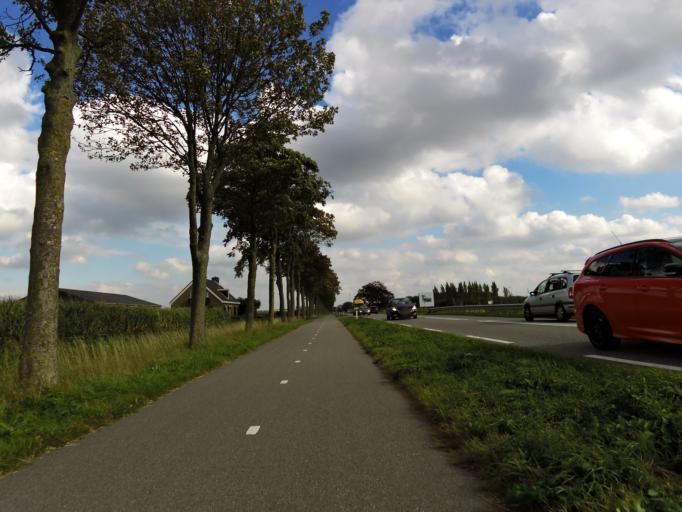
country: NL
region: South Holland
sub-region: Gemeente Waddinxveen
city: Groenswaard
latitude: 52.0771
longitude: 4.6109
